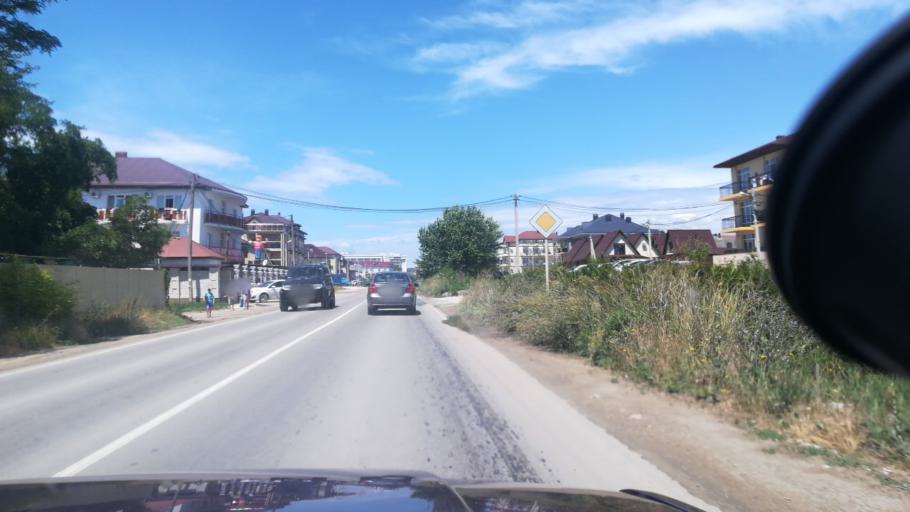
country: RU
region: Krasnodarskiy
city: Vityazevo
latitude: 44.9602
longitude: 37.2952
